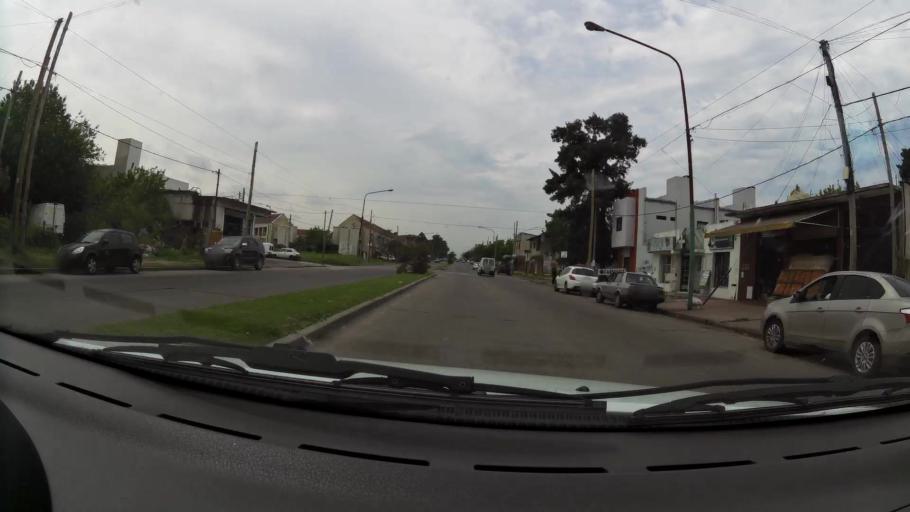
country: AR
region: Buenos Aires
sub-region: Partido de La Plata
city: La Plata
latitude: -34.9048
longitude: -57.9907
